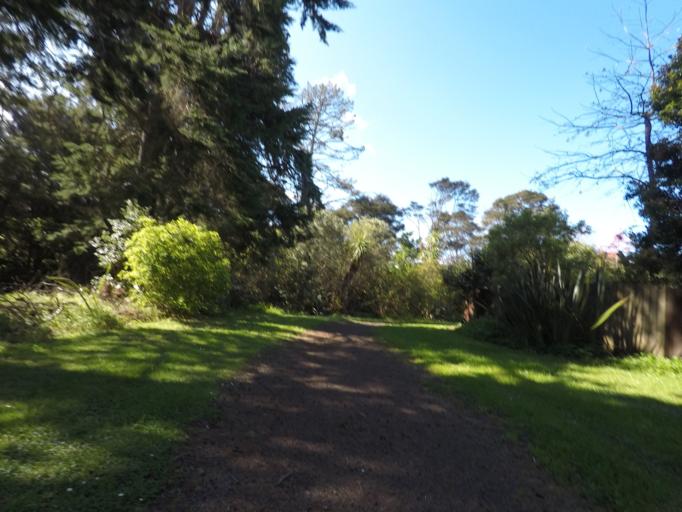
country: NZ
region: Auckland
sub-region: Auckland
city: Rosebank
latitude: -36.8604
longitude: 174.5952
